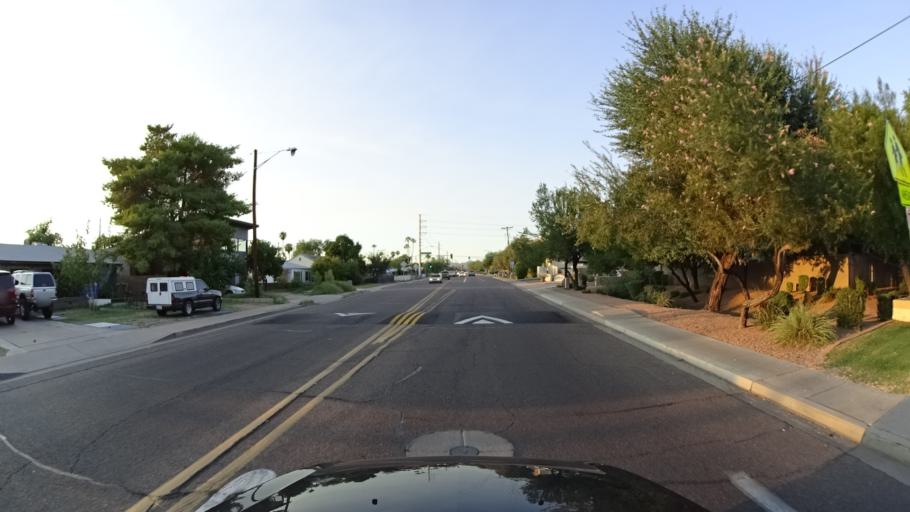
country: US
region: Arizona
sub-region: Maricopa County
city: Phoenix
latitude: 33.5008
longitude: -112.0389
